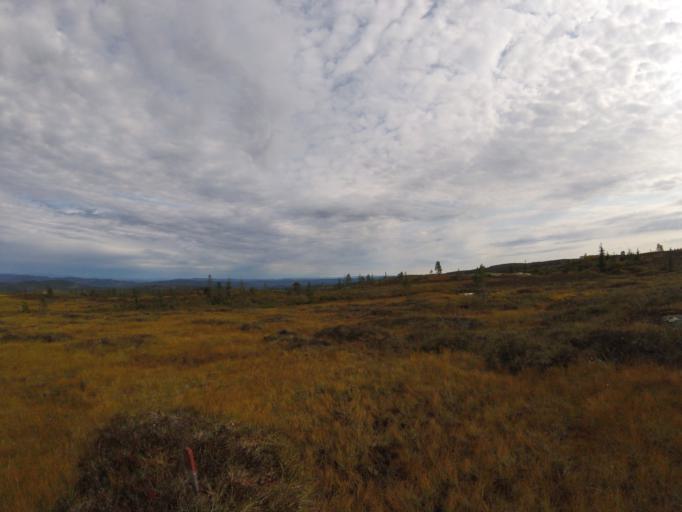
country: NO
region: Buskerud
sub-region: Rollag
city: Rollag
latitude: 59.8093
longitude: 9.3253
